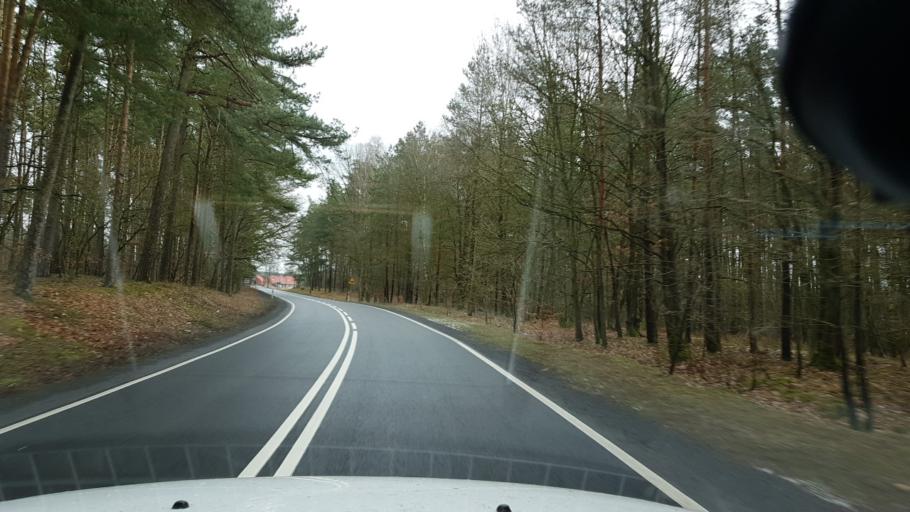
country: PL
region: West Pomeranian Voivodeship
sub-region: Powiat goleniowski
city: Stepnica
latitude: 53.6225
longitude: 14.7269
